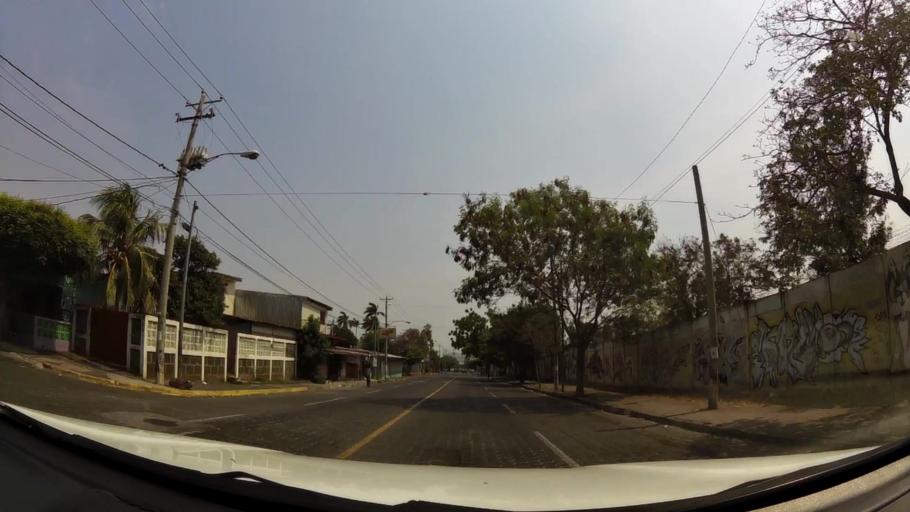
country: NI
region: Managua
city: Ciudad Sandino
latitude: 12.1527
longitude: -86.2972
